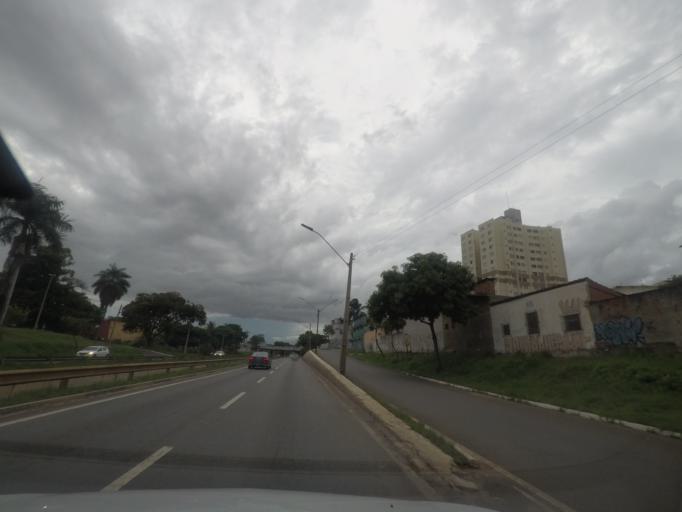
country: BR
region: Goias
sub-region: Goiania
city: Goiania
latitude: -16.6760
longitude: -49.2498
